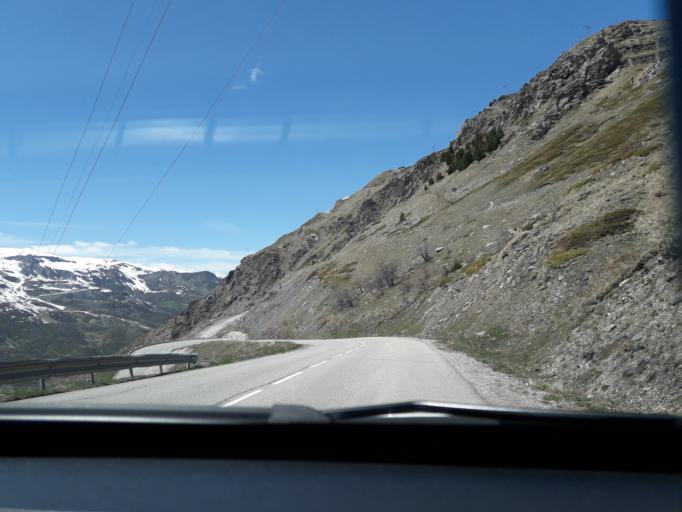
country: FR
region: Rhone-Alpes
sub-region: Departement de la Savoie
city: Val Thorens
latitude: 45.2998
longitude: 6.5671
